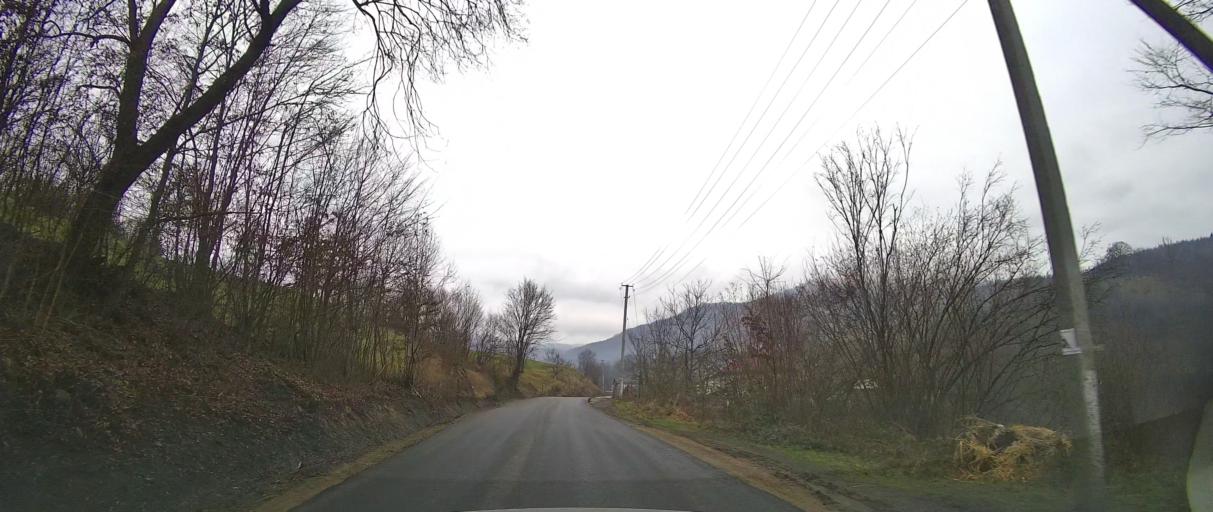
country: UA
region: Zakarpattia
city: Velykyi Bereznyi
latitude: 48.9612
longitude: 22.5488
